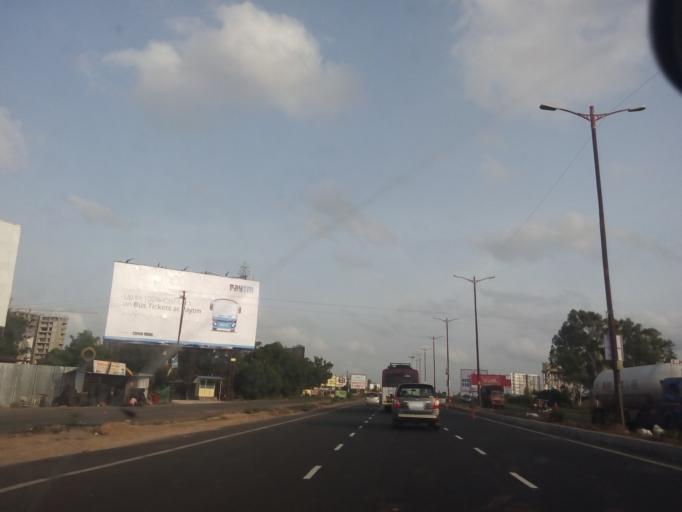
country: IN
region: Maharashtra
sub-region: Pune Division
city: Pimpri
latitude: 18.6368
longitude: 73.7399
